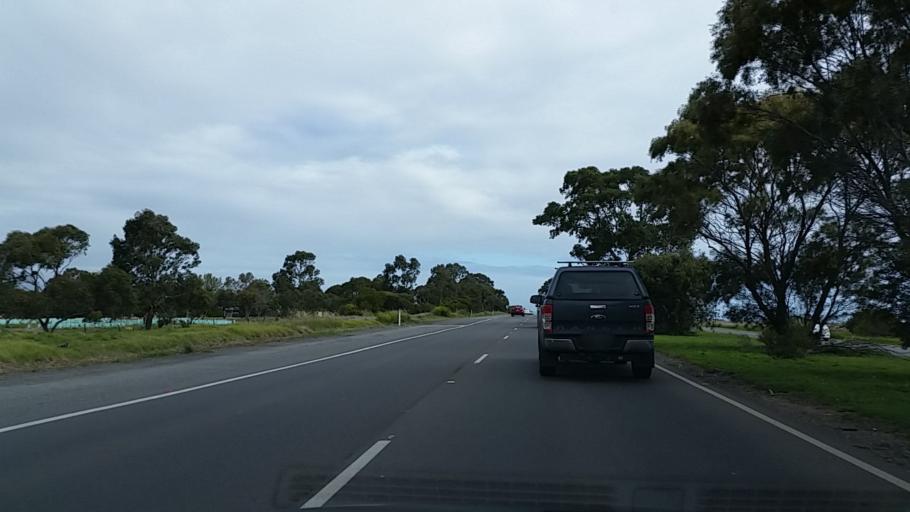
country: AU
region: South Australia
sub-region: Marion
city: Trott Park
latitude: -35.0660
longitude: 138.5320
